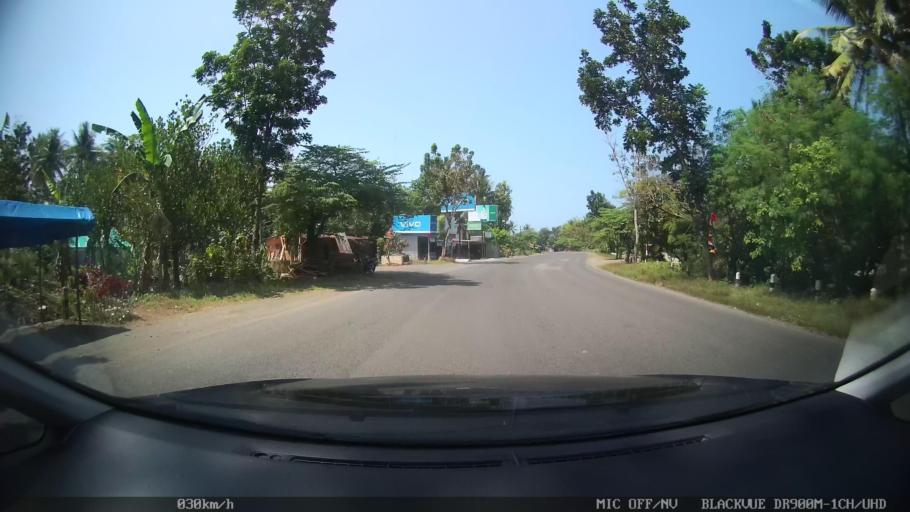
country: ID
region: Daerah Istimewa Yogyakarta
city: Srandakan
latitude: -7.8863
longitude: 110.0462
